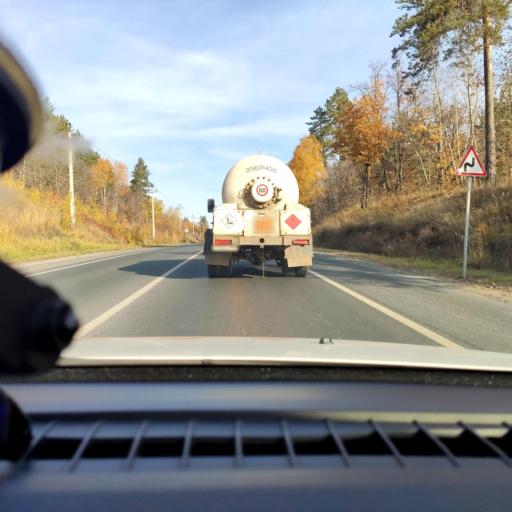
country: RU
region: Samara
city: Volzhskiy
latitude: 53.4444
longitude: 50.1231
